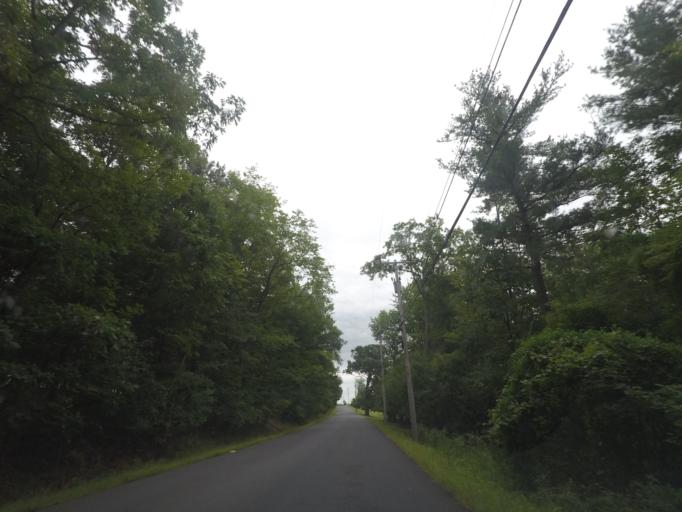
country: US
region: New York
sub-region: Rensselaer County
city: Nassau
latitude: 42.4981
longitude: -73.6043
